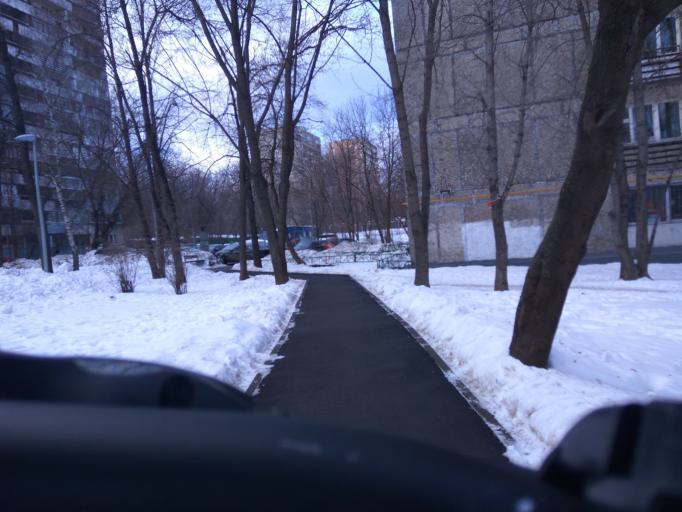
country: RU
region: Moskovskaya
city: Bogorodskoye
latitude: 55.8009
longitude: 37.7296
